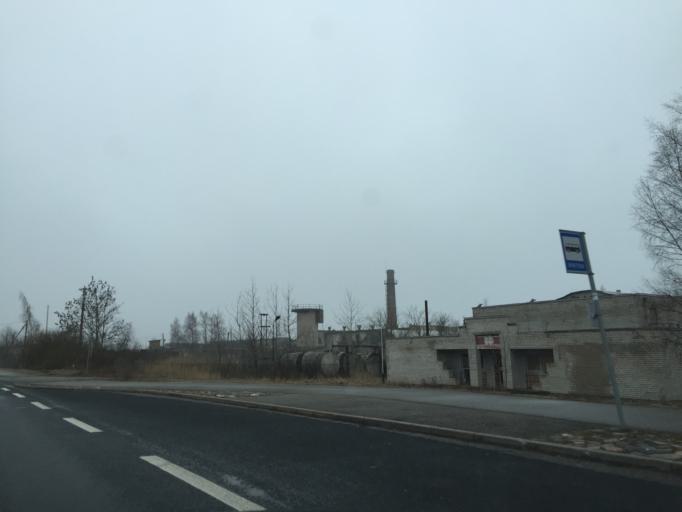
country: EE
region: Laeaene
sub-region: Lihula vald
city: Lihula
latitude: 58.5818
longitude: 23.5246
